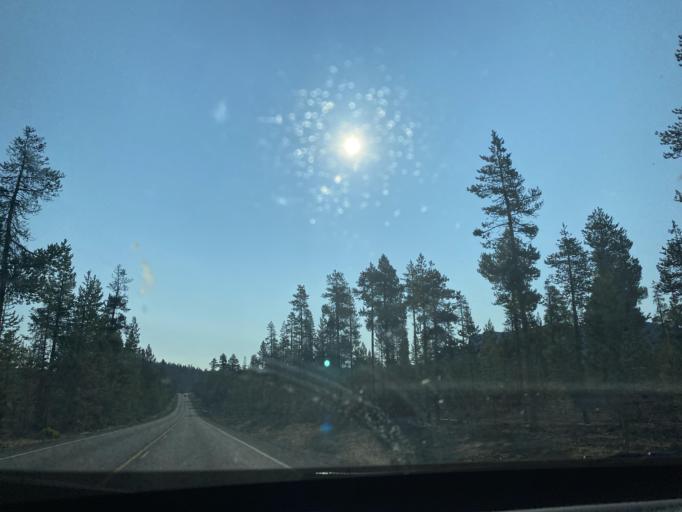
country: US
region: Oregon
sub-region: Deschutes County
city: Three Rivers
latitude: 43.7045
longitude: -121.3080
